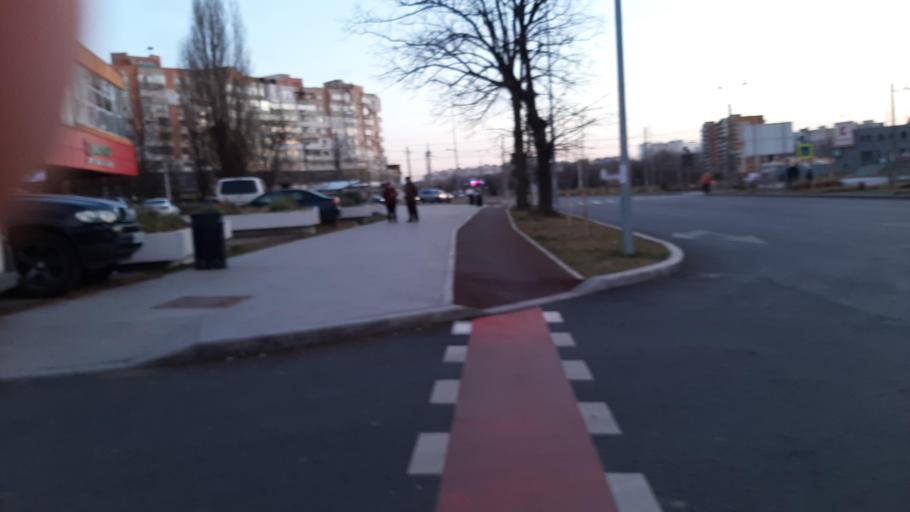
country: RO
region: Galati
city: Galati
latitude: 45.4285
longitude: 28.0249
